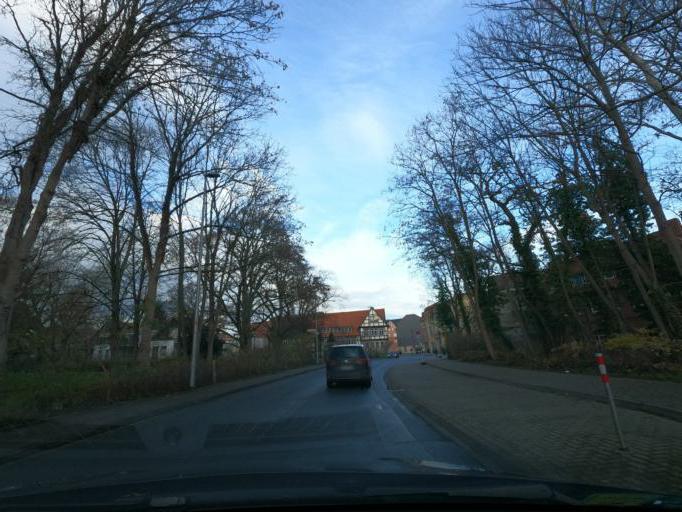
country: DE
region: Lower Saxony
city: Wolfenbuettel
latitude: 52.1612
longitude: 10.5327
